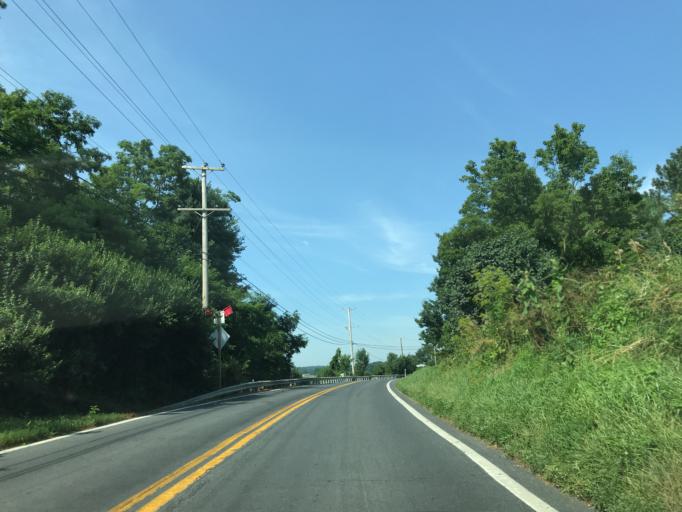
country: US
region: Maryland
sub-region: Carroll County
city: Manchester
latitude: 39.6637
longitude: -76.9463
